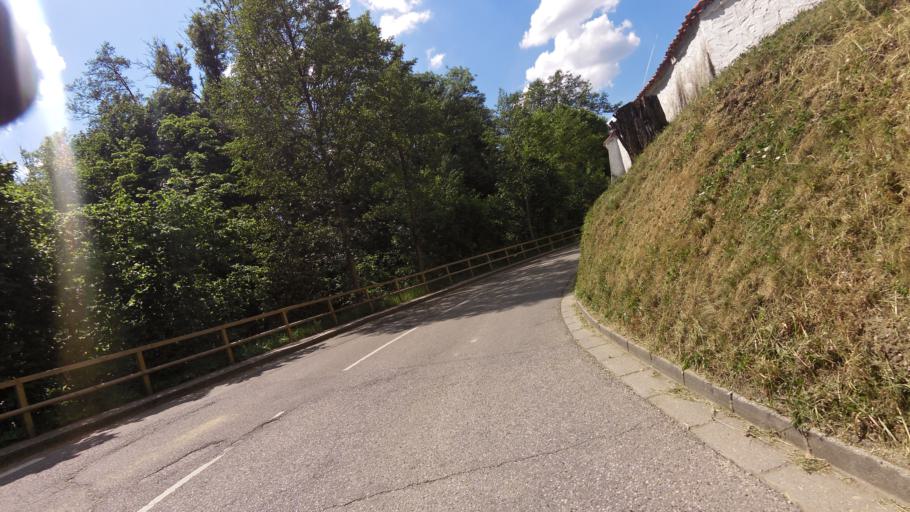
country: DE
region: Bavaria
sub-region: Upper Bavaria
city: Wang
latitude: 48.4944
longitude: 11.9370
